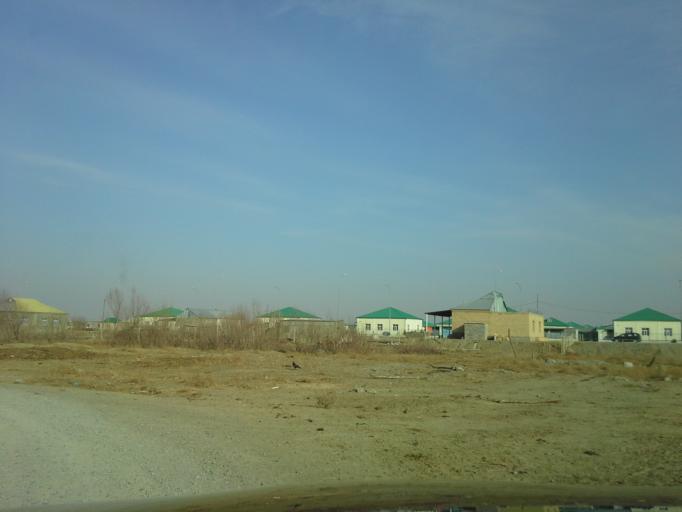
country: TM
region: Ahal
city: Abadan
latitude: 38.1740
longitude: 58.0461
